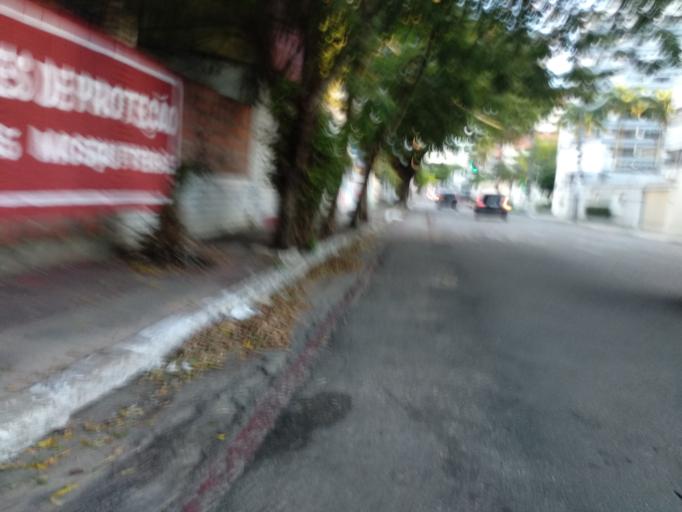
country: BR
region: Ceara
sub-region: Fortaleza
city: Fortaleza
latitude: -3.7363
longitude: -38.5095
